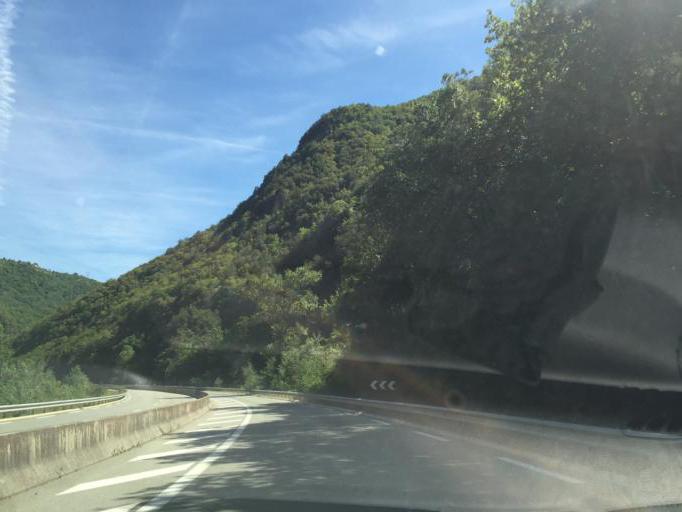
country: FR
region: Provence-Alpes-Cote d'Azur
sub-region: Departement des Alpes-Maritimes
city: Saint-Martin-Vesubie
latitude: 44.0111
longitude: 7.1316
